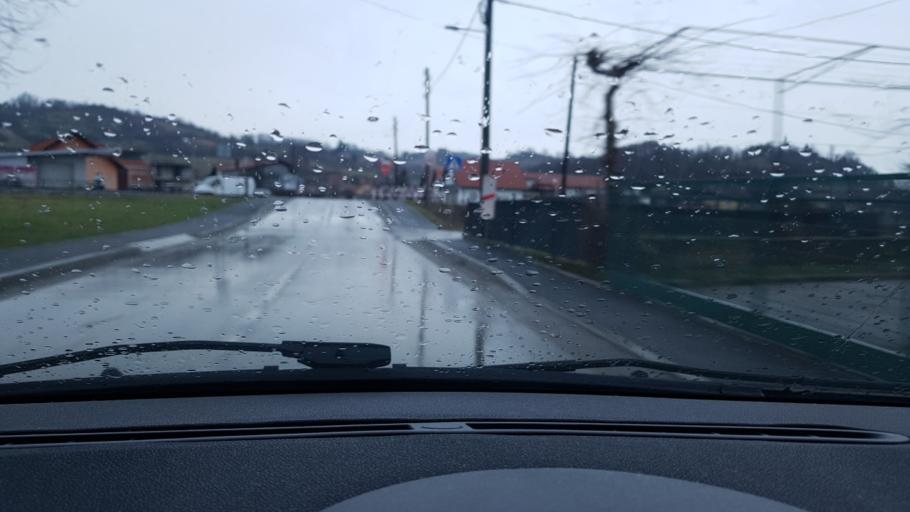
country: HR
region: Krapinsko-Zagorska
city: Oroslavje
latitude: 45.9830
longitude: 15.9737
